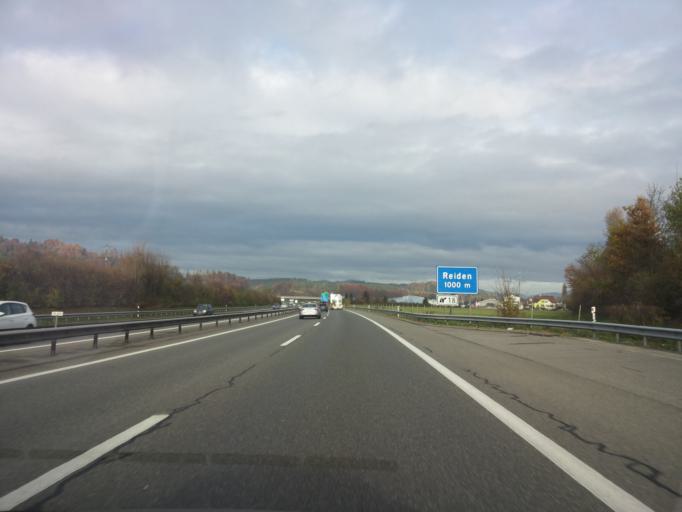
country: CH
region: Lucerne
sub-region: Willisau District
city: Reiden
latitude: 47.2335
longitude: 7.9683
